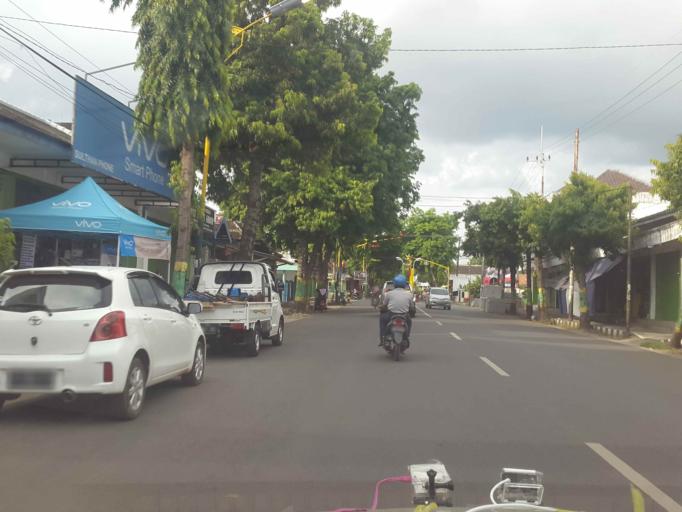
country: ID
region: East Java
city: Sumenep
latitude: -7.0033
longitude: 113.8608
